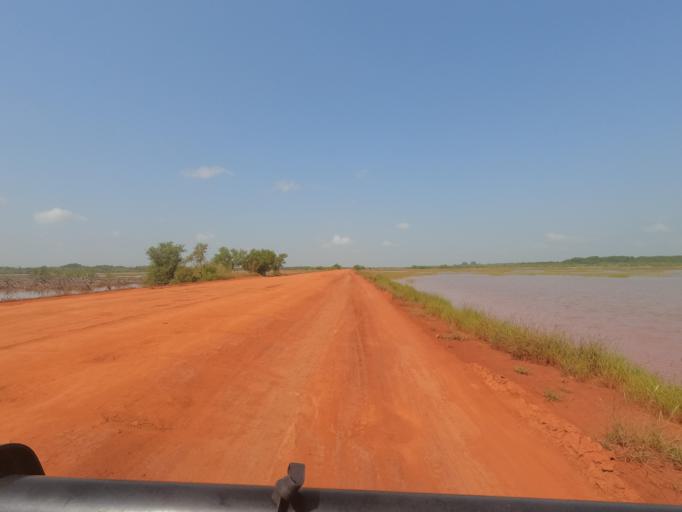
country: GW
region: Cacheu
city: Canchungo
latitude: 12.2544
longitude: -15.7728
